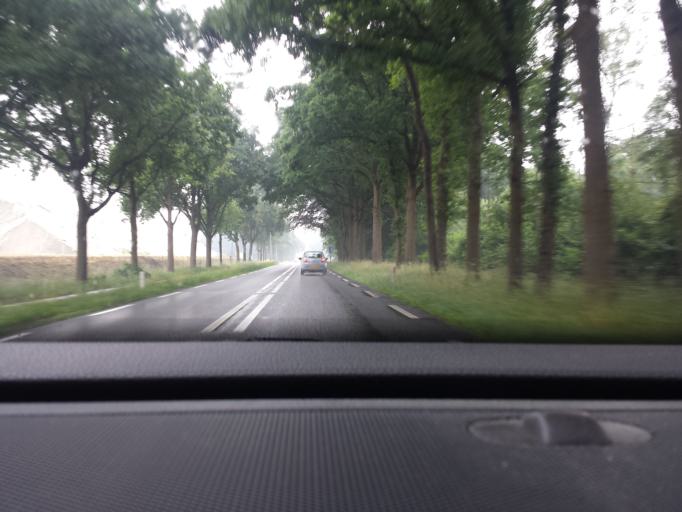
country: NL
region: Overijssel
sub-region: Gemeente Haaksbergen
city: Haaksbergen
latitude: 52.1789
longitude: 6.7941
